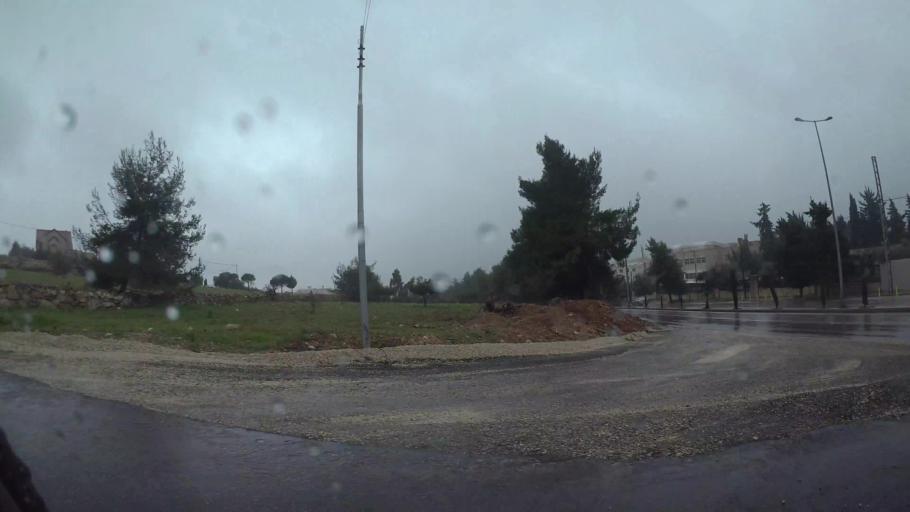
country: JO
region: Amman
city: Wadi as Sir
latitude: 31.9971
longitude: 35.8121
